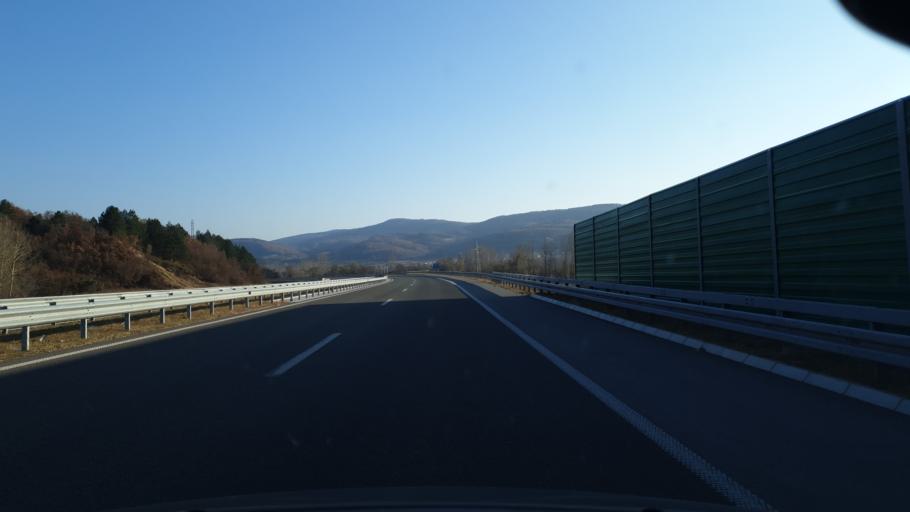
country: RS
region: Central Serbia
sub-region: Pirotski Okrug
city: Dimitrovgrad
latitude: 43.0286
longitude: 22.7229
